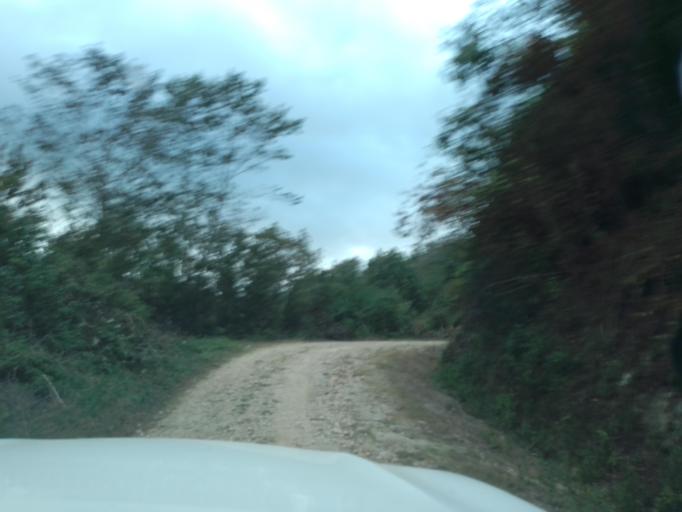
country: MX
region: Chiapas
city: Motozintla de Mendoza
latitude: 15.2110
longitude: -92.2258
